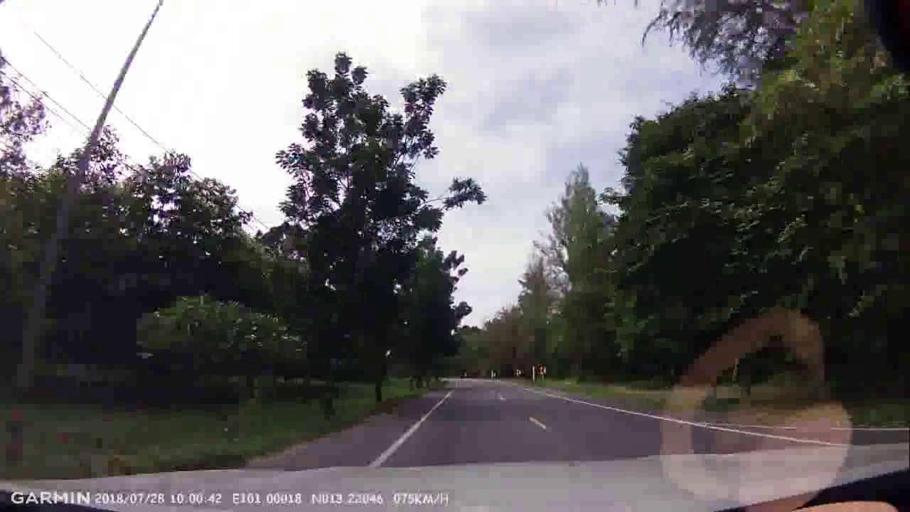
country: TH
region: Chon Buri
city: Si Racha
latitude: 13.2202
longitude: 101.0002
